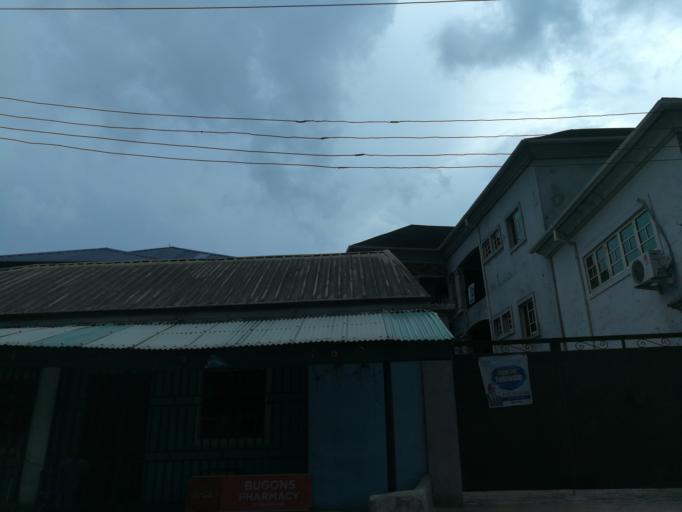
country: NG
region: Rivers
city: Port Harcourt
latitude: 4.8172
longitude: 7.0682
